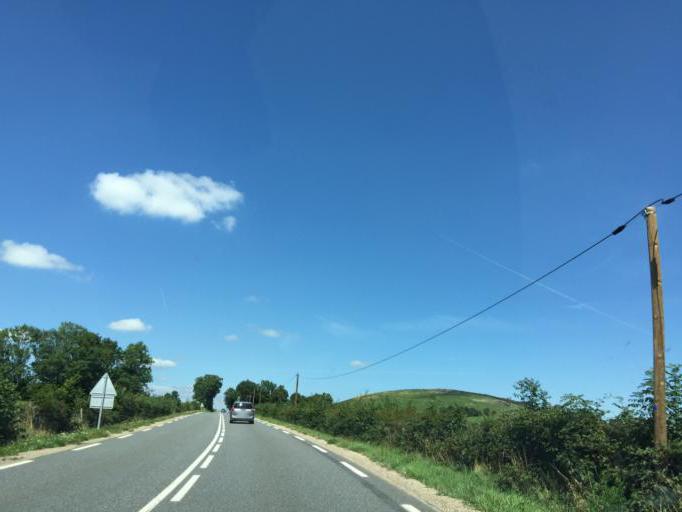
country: FR
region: Midi-Pyrenees
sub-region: Departement de l'Aveyron
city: Laguiole
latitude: 44.6181
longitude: 2.8154
